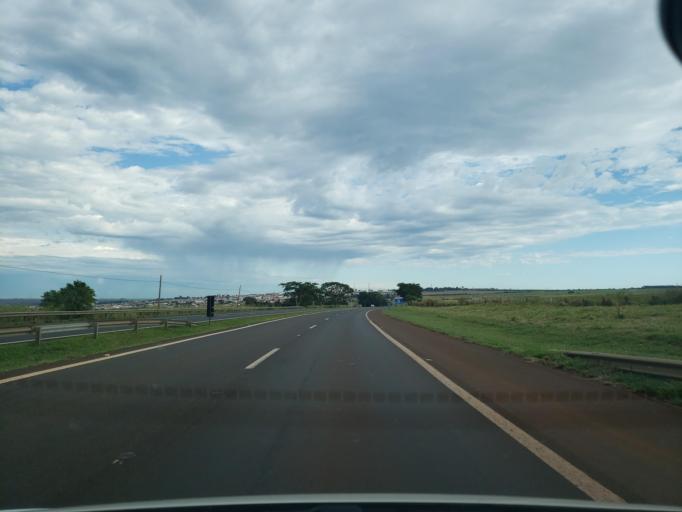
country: BR
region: Sao Paulo
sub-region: Jau
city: Jau
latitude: -22.2643
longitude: -48.5243
